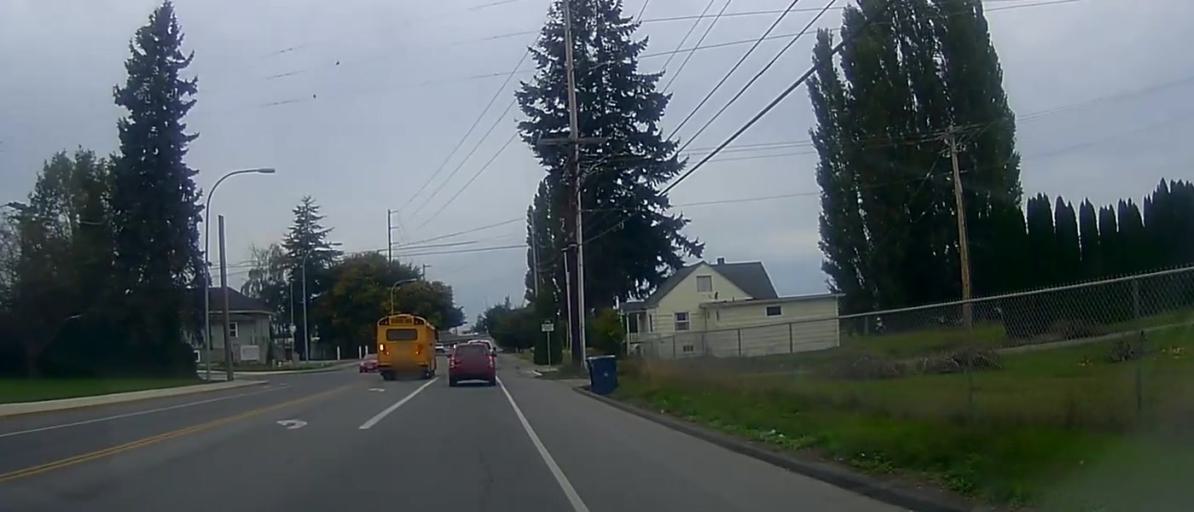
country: US
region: Washington
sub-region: Skagit County
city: Mount Vernon
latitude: 48.4431
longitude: -122.3315
